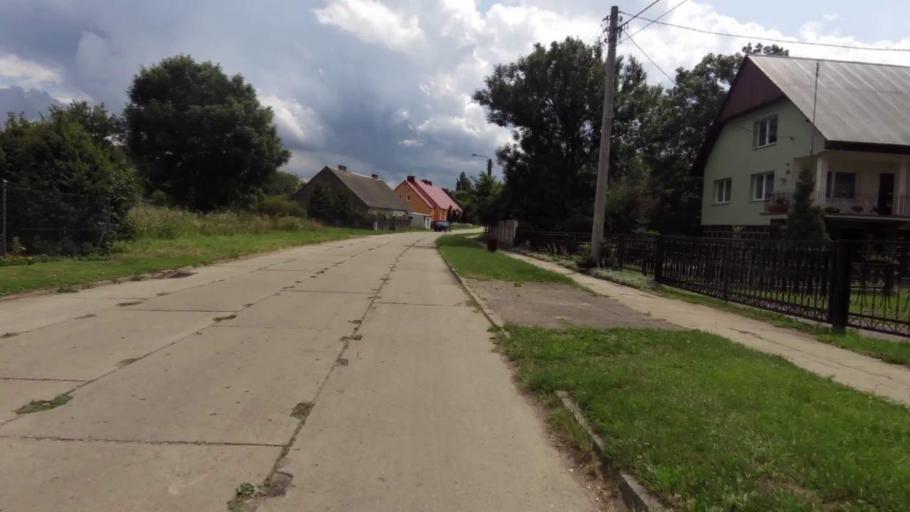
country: PL
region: West Pomeranian Voivodeship
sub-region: Powiat mysliborski
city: Nowogrodek Pomorski
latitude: 52.9898
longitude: 15.0592
